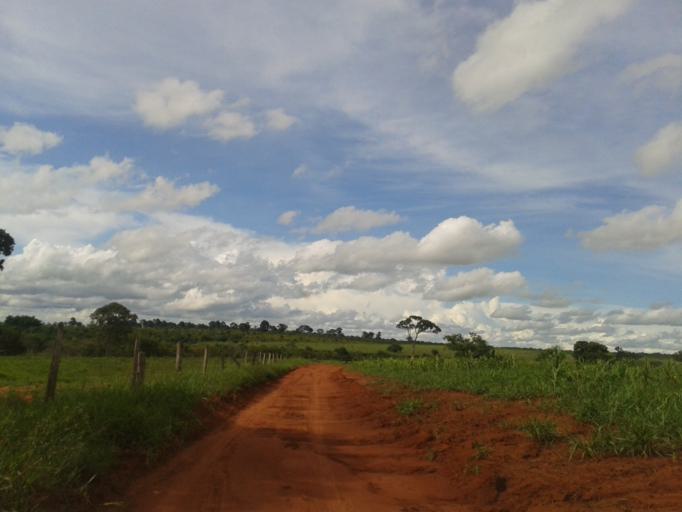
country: BR
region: Minas Gerais
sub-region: Santa Vitoria
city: Santa Vitoria
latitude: -19.1358
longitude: -50.4864
